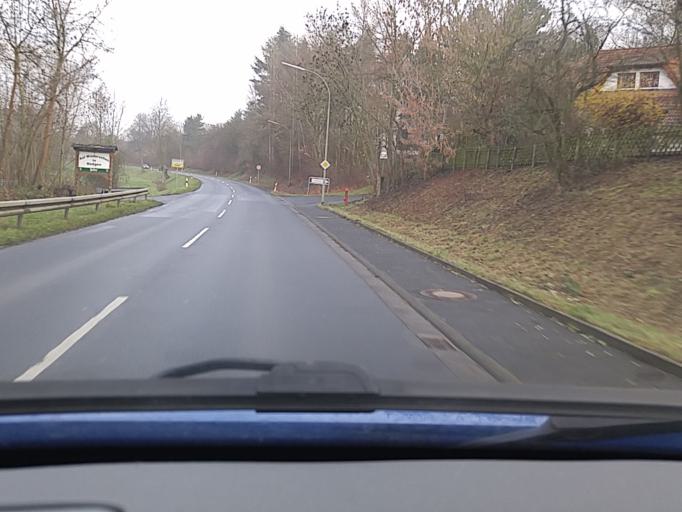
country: DE
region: Hesse
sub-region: Regierungsbezirk Darmstadt
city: Bad Nauheim
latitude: 50.3690
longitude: 8.7642
